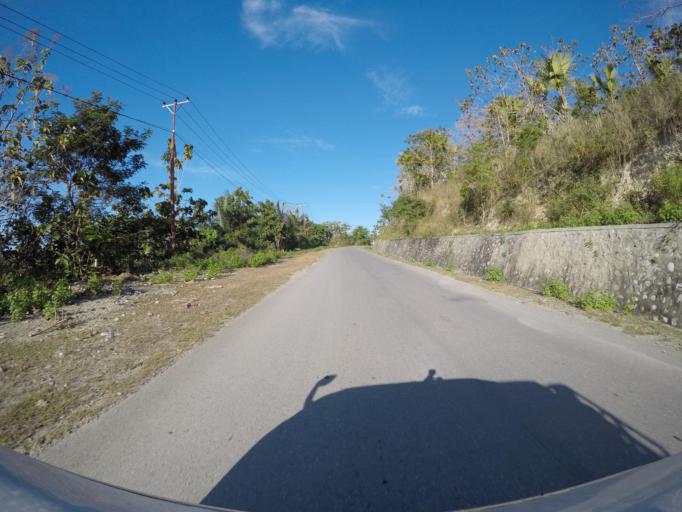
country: TL
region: Viqueque
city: Viqueque
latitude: -8.8714
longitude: 126.3530
